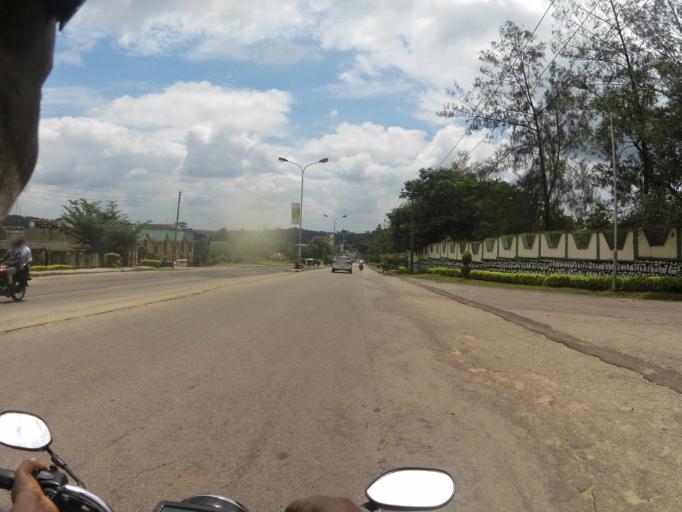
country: NG
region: Oyo
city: Ibadan
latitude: 7.4071
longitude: 3.9076
